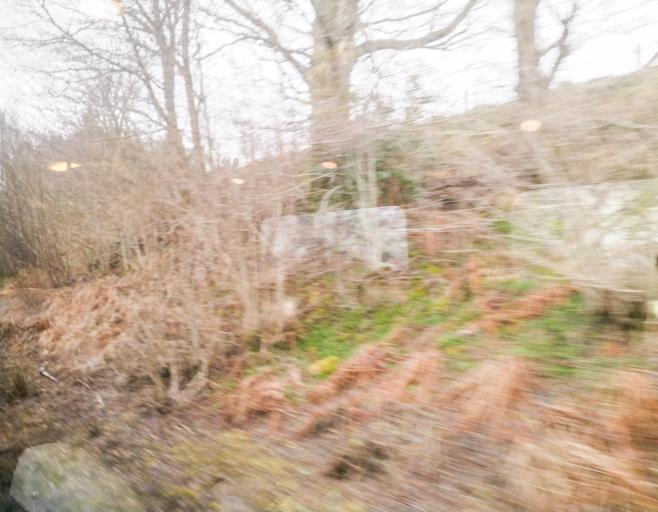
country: GB
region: Scotland
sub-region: Highland
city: Spean Bridge
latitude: 56.8882
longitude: -4.8609
